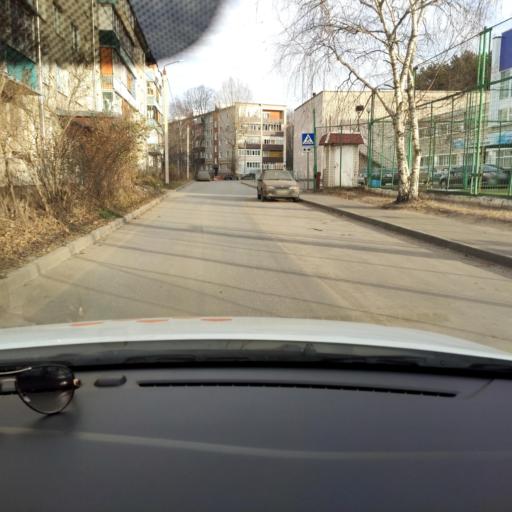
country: RU
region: Tatarstan
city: Vysokaya Gora
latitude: 55.8582
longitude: 49.2247
